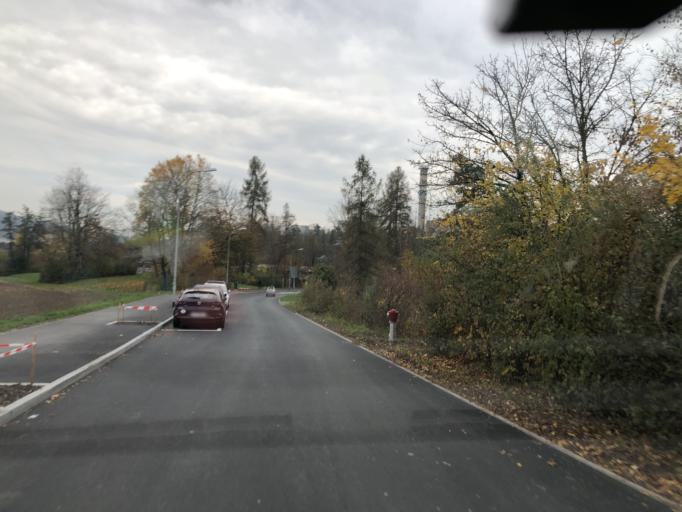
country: CH
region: Aargau
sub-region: Bezirk Baden
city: Birmenstorf
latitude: 47.4599
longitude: 8.2784
